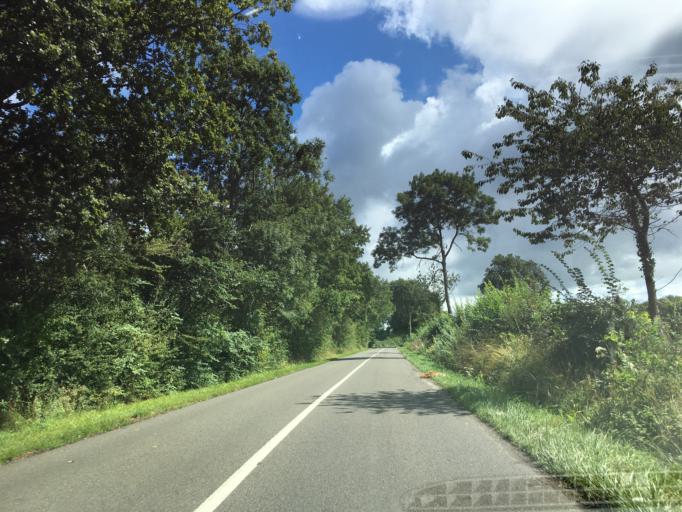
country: FR
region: Lower Normandy
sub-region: Departement du Calvados
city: Houlgate
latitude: 49.2736
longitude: -0.0520
